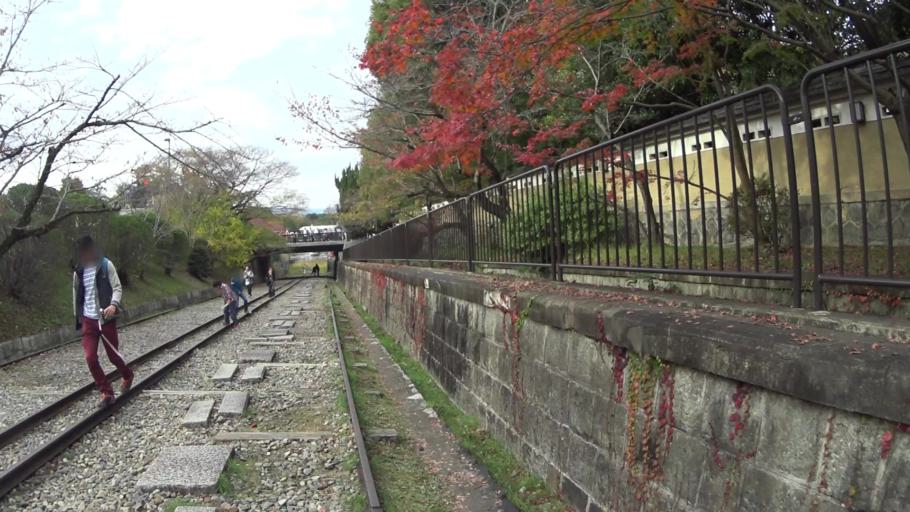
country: JP
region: Kyoto
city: Kyoto
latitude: 35.0108
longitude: 135.7888
